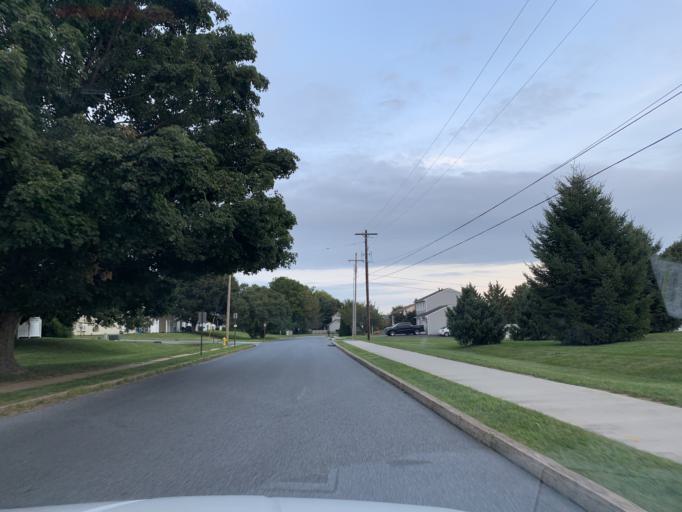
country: US
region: Pennsylvania
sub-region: York County
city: Emigsville
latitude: 40.0067
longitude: -76.7305
